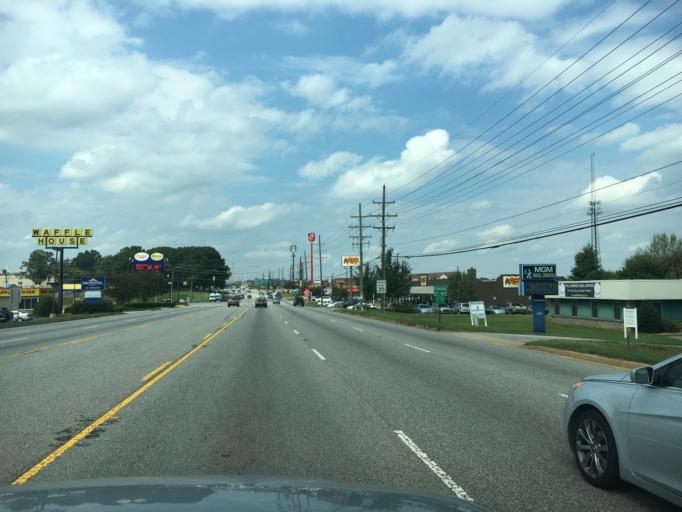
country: US
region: South Carolina
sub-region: Spartanburg County
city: Wellford
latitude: 34.9092
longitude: -82.1024
